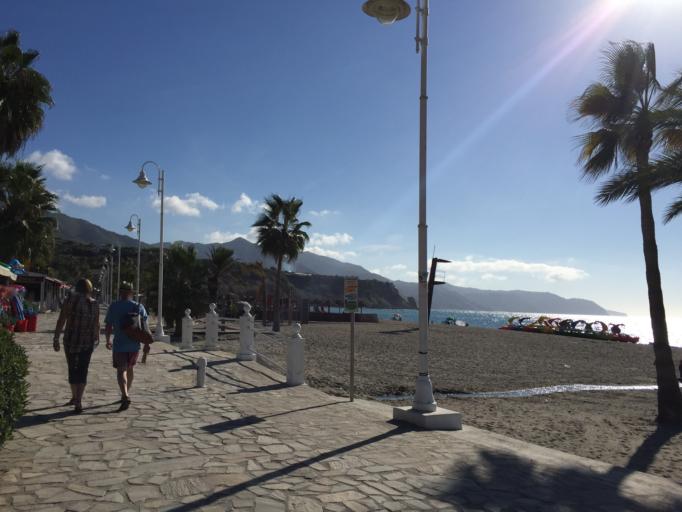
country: ES
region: Andalusia
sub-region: Provincia de Malaga
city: Nerja
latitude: 36.7498
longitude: -3.8687
